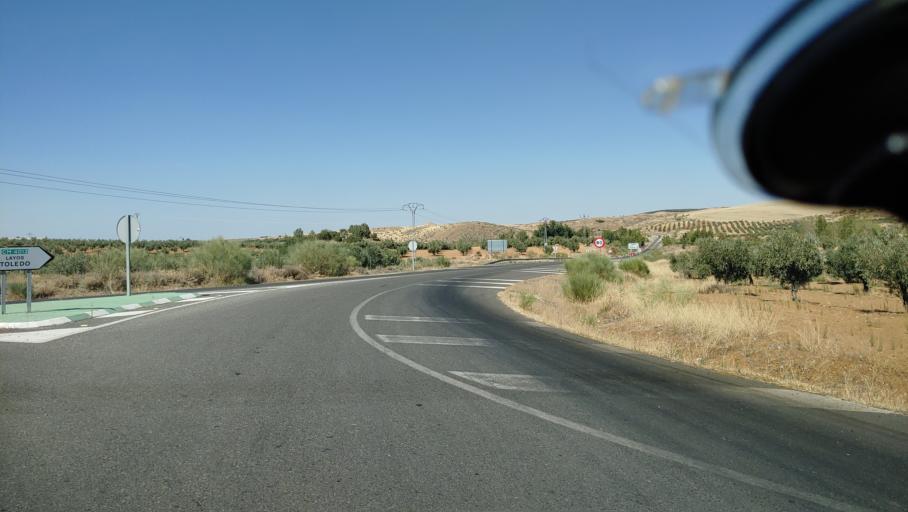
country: ES
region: Castille-La Mancha
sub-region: Province of Toledo
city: Casasbuenas
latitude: 39.7405
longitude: -4.0961
